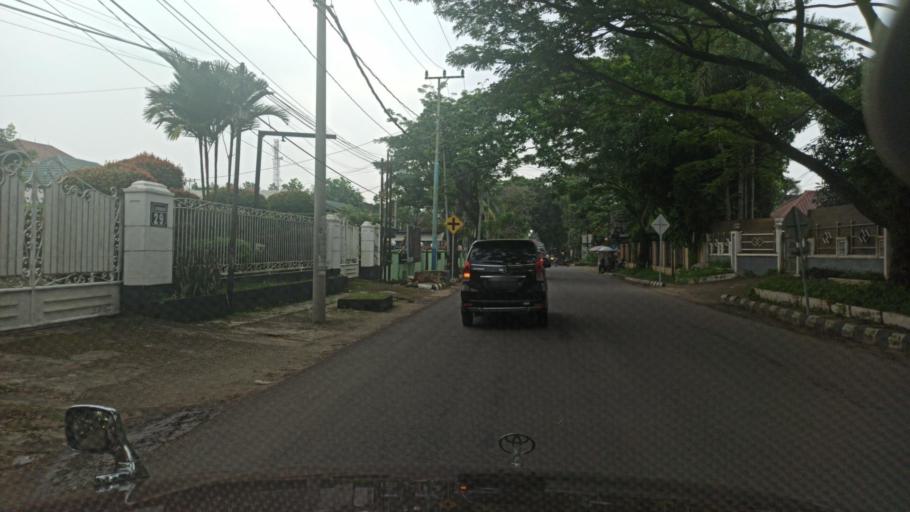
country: ID
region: South Sumatra
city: Plaju
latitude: -2.9929
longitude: 104.7493
